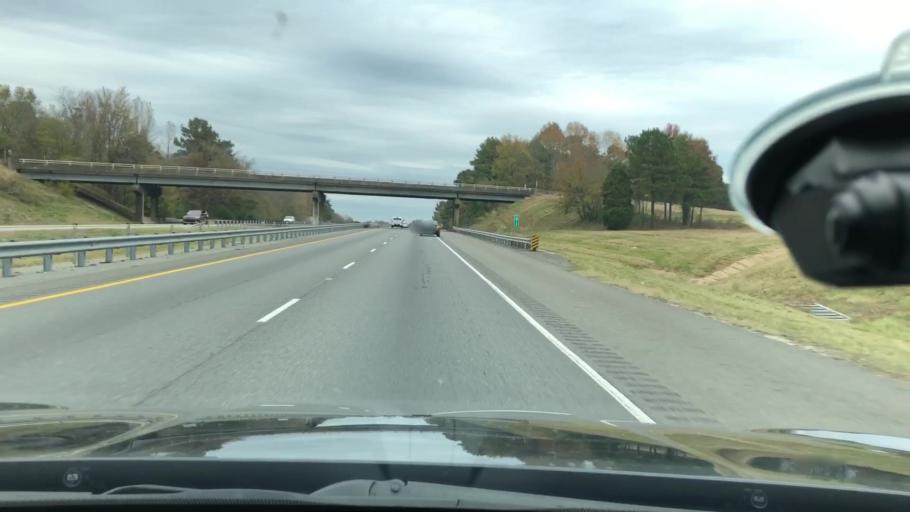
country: US
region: Arkansas
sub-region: Hot Spring County
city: Malvern
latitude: 34.3325
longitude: -92.9195
